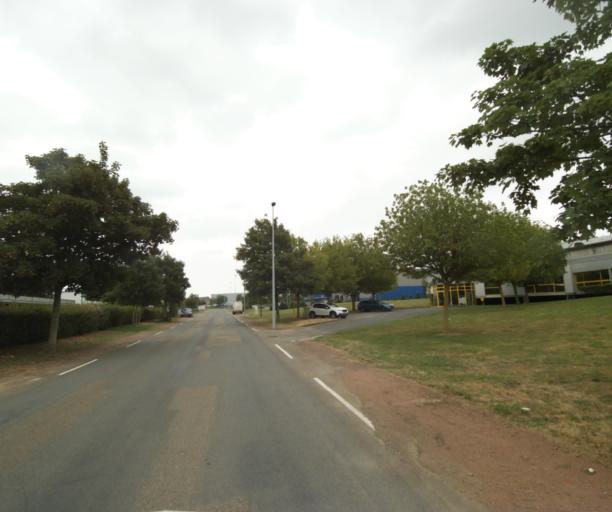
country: FR
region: Pays de la Loire
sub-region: Departement de la Sarthe
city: Solesmes
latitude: 47.8349
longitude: -0.2963
